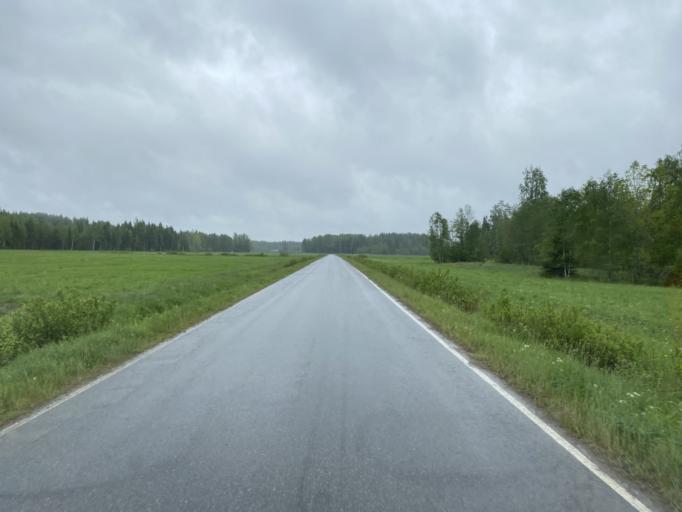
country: FI
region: Haeme
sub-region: Forssa
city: Humppila
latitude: 61.0522
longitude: 23.3428
